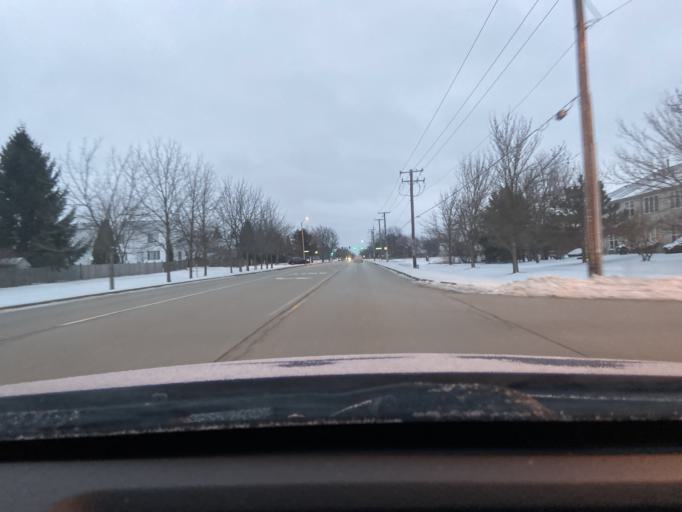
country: US
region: Illinois
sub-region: Lake County
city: Grayslake
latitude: 42.3539
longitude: -88.0241
